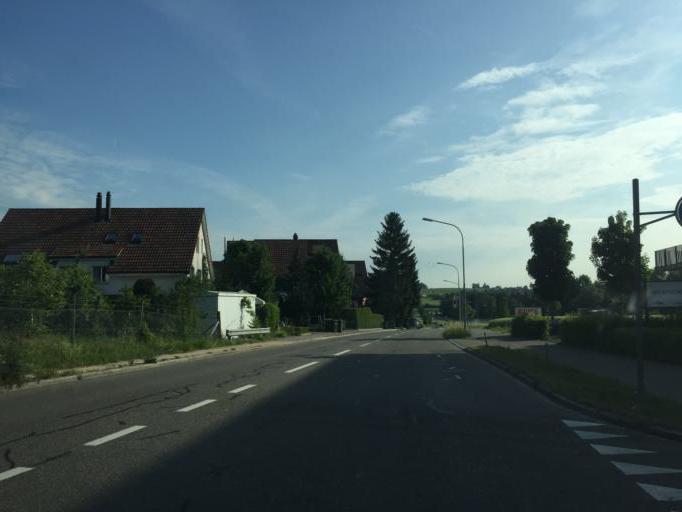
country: CH
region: Zurich
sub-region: Bezirk Zuerich
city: Zuerich (Kreis 11) / Affoltern
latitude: 47.4256
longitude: 8.5094
